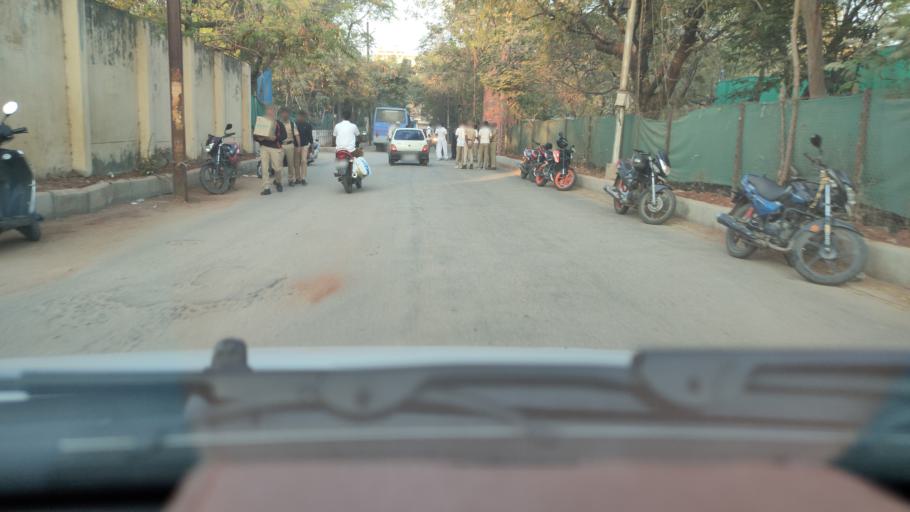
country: IN
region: Telangana
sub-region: Rangareddi
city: Gaddi Annaram
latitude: 17.3868
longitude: 78.5180
